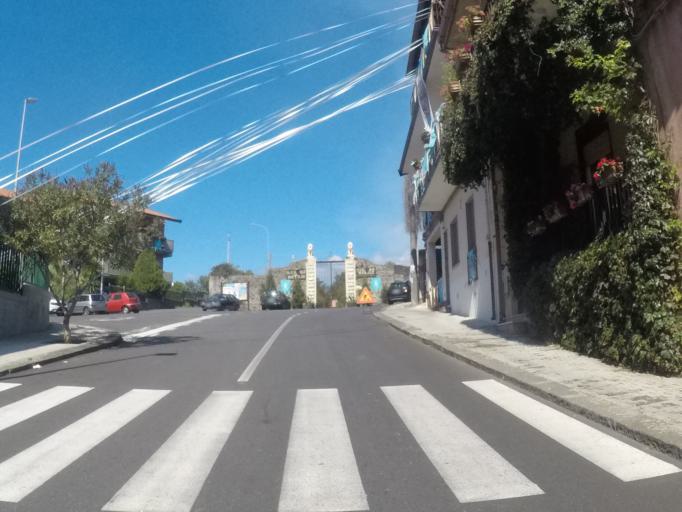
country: IT
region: Sicily
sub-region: Catania
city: Belpasso
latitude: 37.6056
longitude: 14.9846
